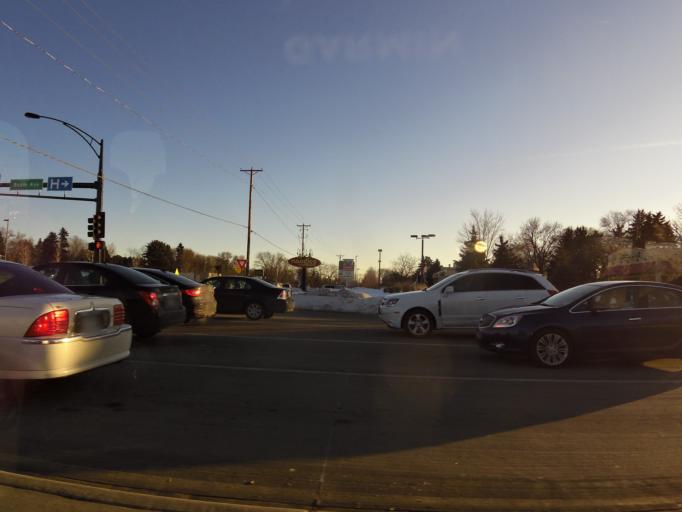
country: US
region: Minnesota
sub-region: Ramsey County
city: North Saint Paul
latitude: 45.0281
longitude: -93.0183
